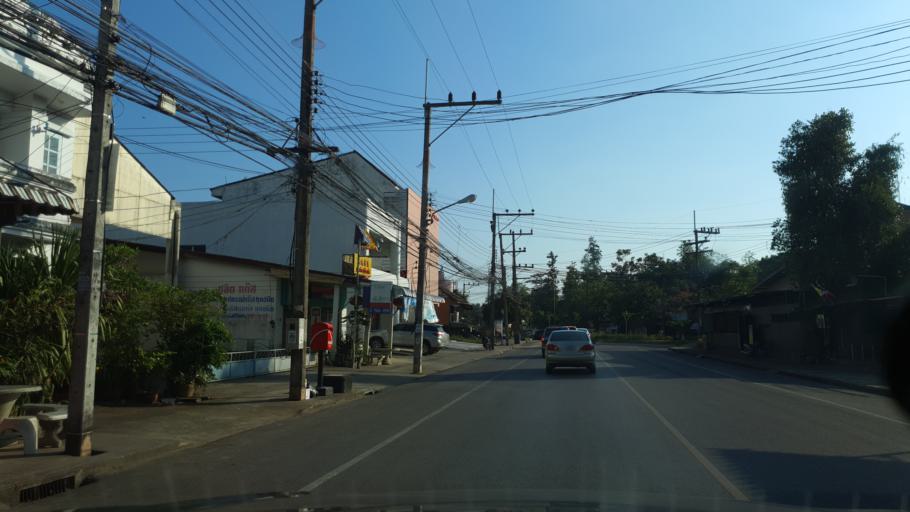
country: TH
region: Krabi
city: Krabi
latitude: 8.1002
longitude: 98.9111
